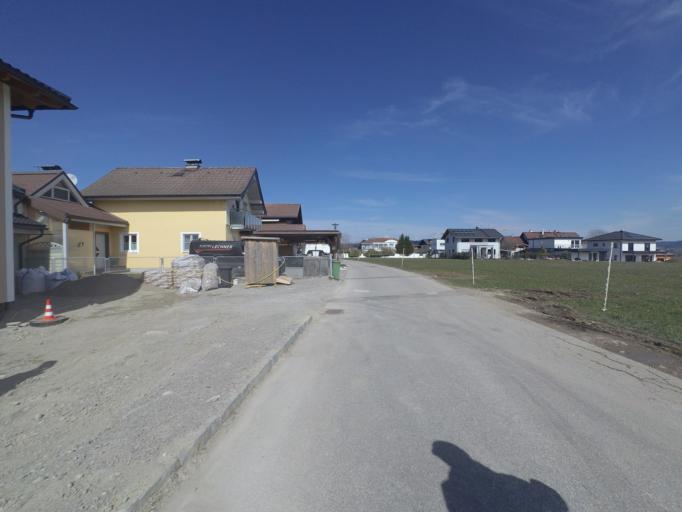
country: AT
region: Salzburg
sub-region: Politischer Bezirk Salzburg-Umgebung
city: Seekirchen am Wallersee
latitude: 47.8963
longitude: 13.1138
